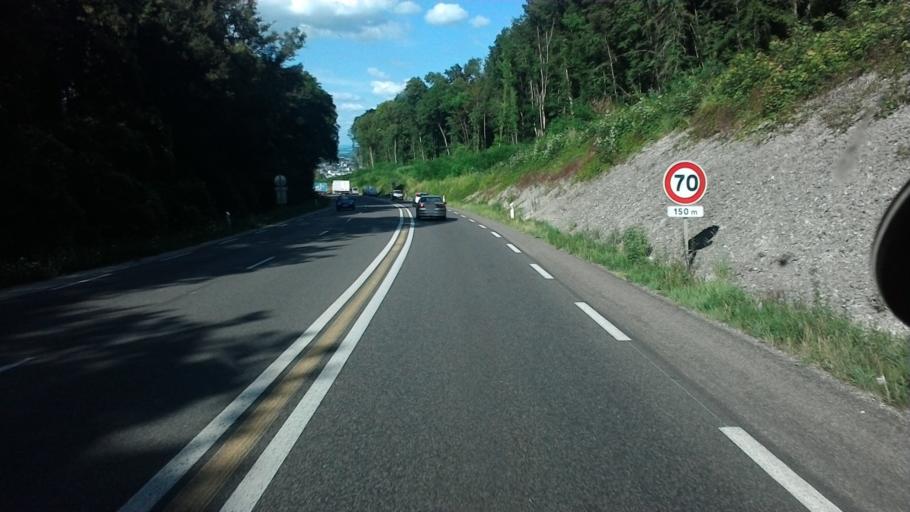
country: FR
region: Franche-Comte
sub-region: Departement de la Haute-Saone
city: Noidans-les-Vesoul
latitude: 47.6028
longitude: 6.1182
